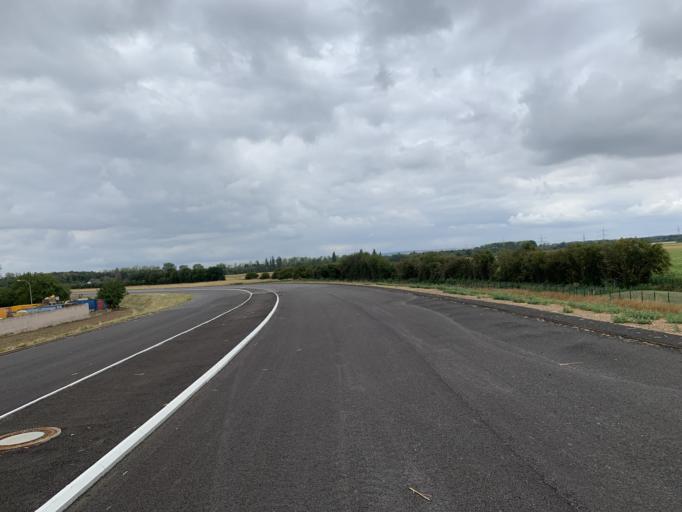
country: DE
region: North Rhine-Westphalia
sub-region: Regierungsbezirk Koln
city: Merzenich
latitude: 50.8166
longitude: 6.5111
